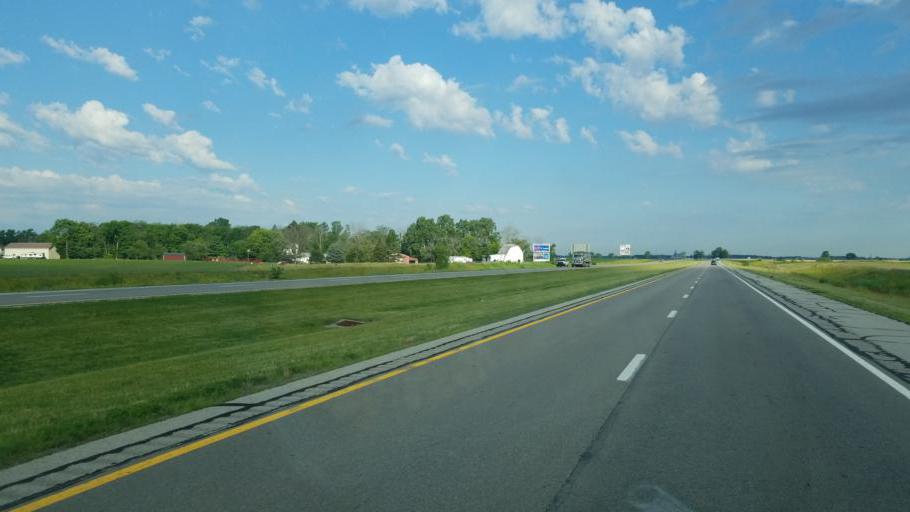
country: US
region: Ohio
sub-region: Crawford County
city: Galion
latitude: 40.7704
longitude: -82.8779
